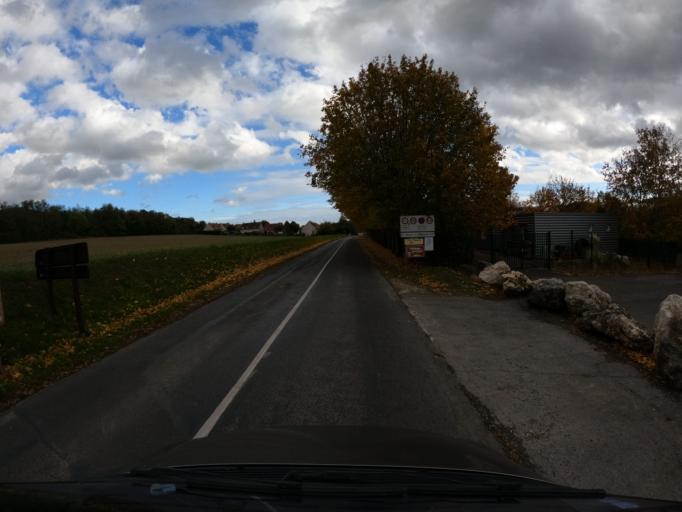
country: FR
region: Ile-de-France
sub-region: Departement de Seine-et-Marne
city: Coupvray
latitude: 48.8991
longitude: 2.7863
